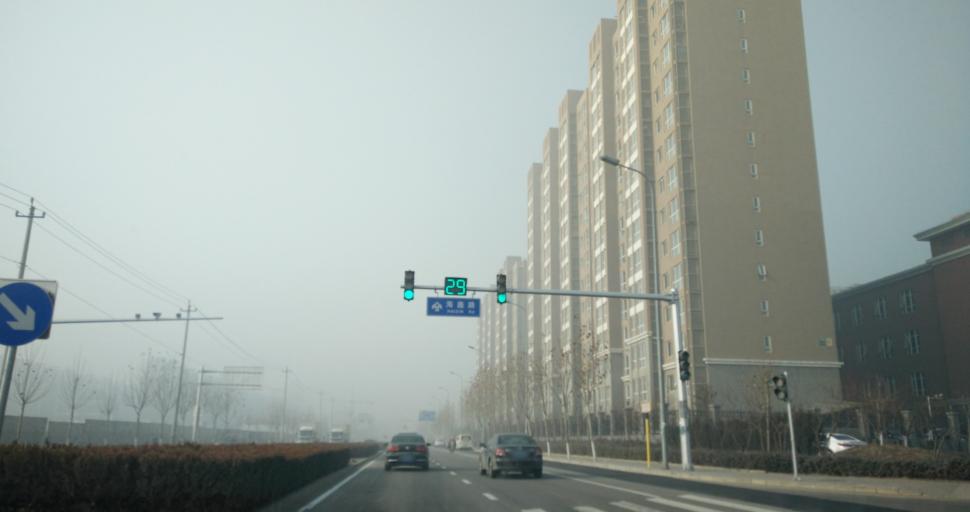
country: CN
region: Beijing
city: Yinghai
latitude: 39.7085
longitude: 116.4009
